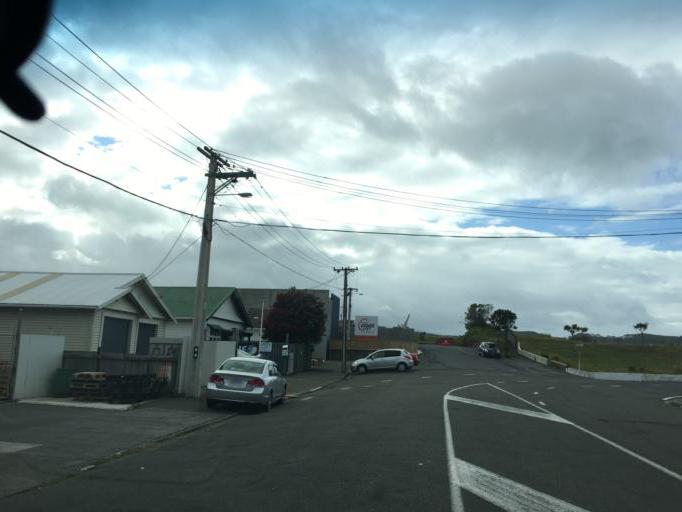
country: NZ
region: Wellington
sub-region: Wellington City
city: Wellington
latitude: -41.3193
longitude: 174.8053
